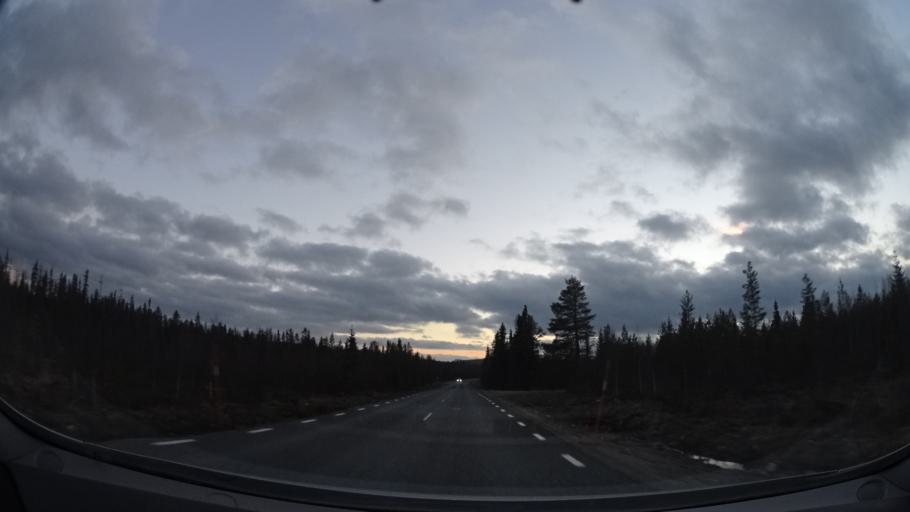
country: SE
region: Vaesterbotten
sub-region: Asele Kommun
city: Insjon
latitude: 64.3031
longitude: 17.6873
